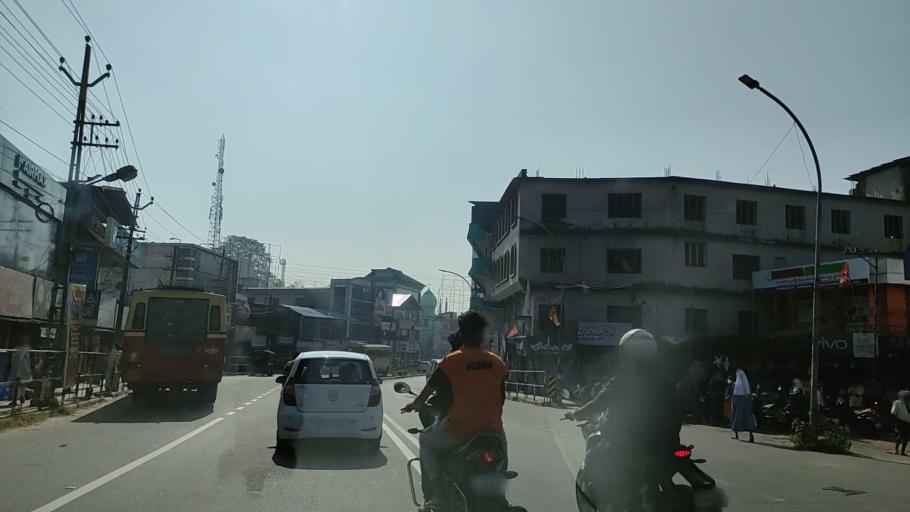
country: IN
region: Kerala
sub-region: Kollam
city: Punalur
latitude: 8.8987
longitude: 76.8598
